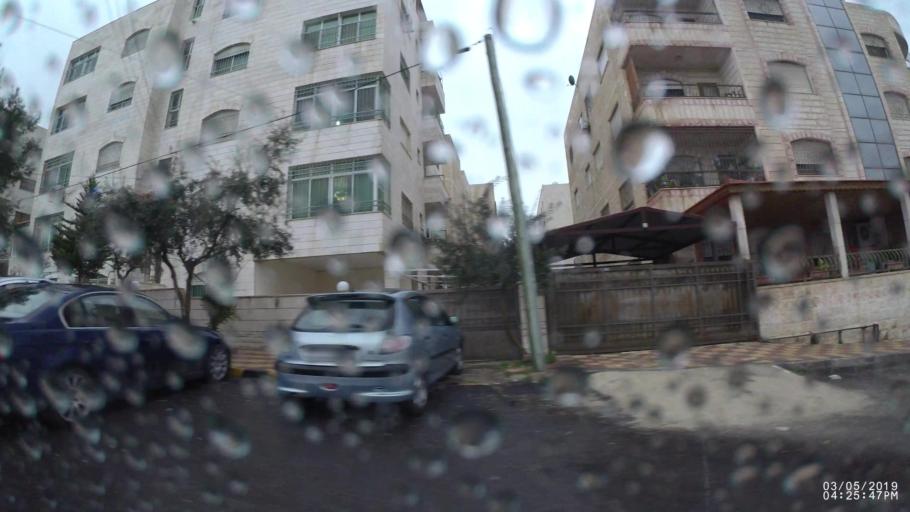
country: JO
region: Amman
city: Amman
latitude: 32.0033
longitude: 35.9620
